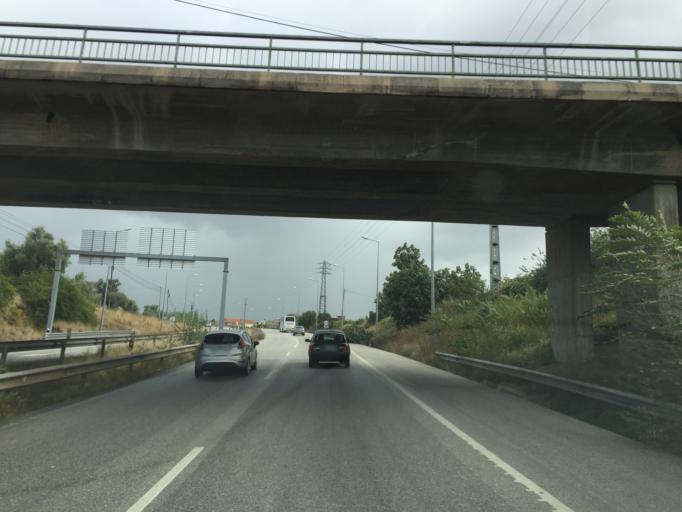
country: PT
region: Coimbra
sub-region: Coimbra
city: Coimbra
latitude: 40.2011
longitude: -8.4857
